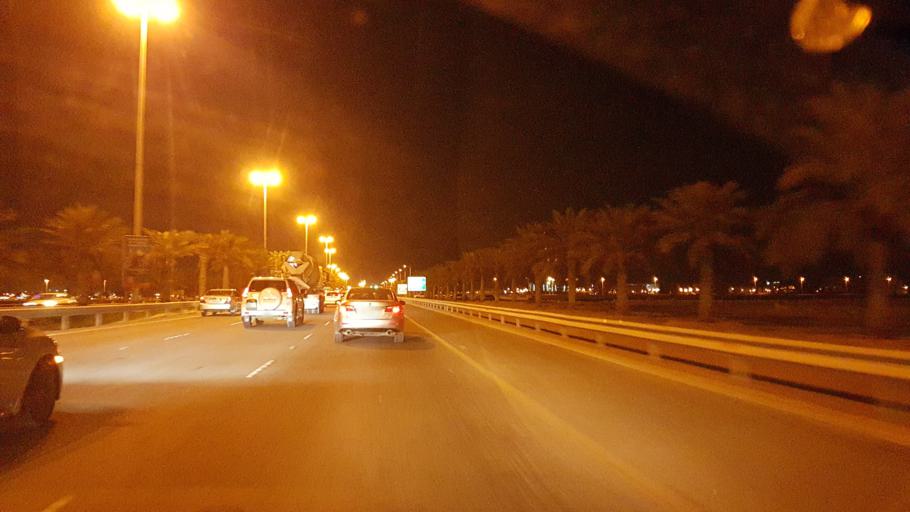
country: BH
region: Muharraq
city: Al Hadd
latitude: 26.2497
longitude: 50.6592
